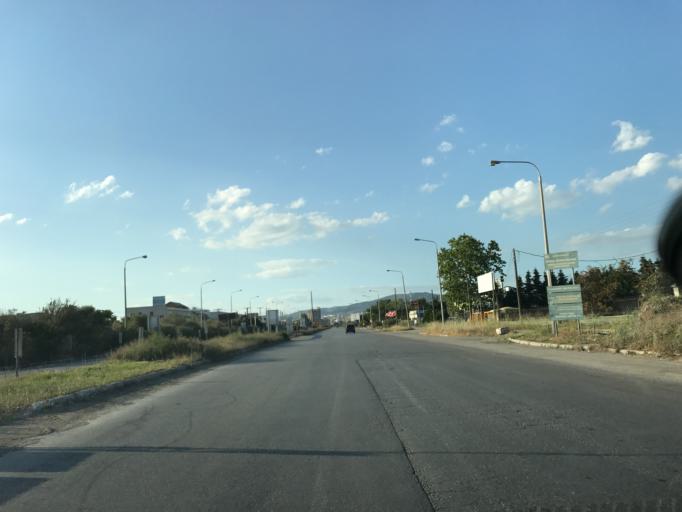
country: GR
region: Central Macedonia
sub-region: Nomos Thessalonikis
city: Menemeni
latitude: 40.6579
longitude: 22.8820
